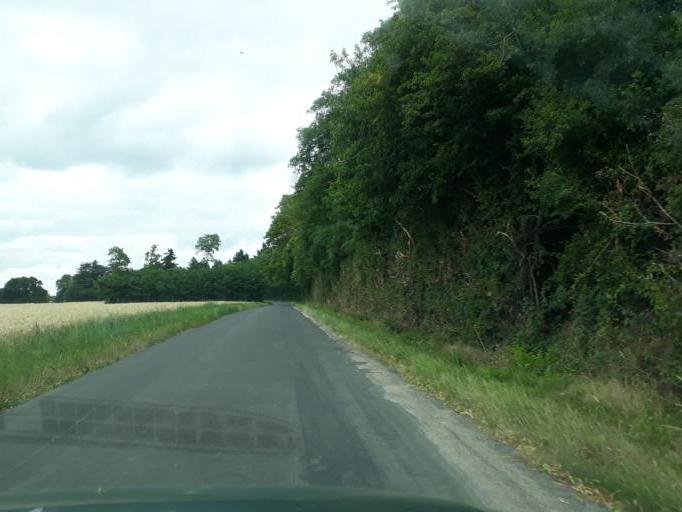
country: FR
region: Centre
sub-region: Departement du Loiret
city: Sandillon
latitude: 47.8425
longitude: 2.0002
